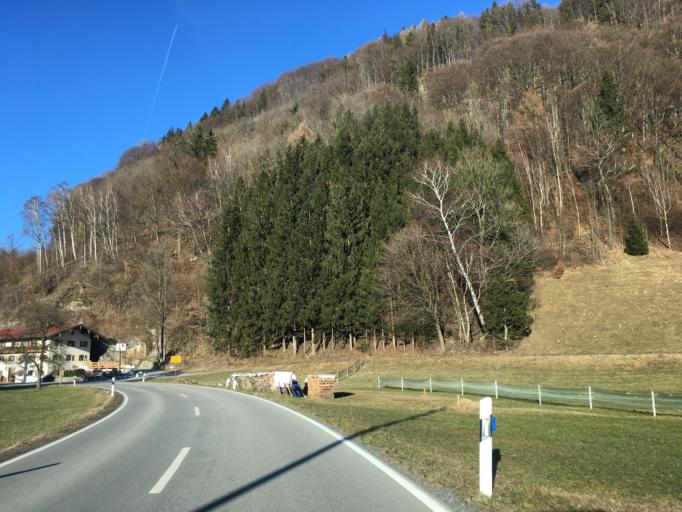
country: AT
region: Tyrol
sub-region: Politischer Bezirk Kufstein
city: Erl
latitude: 47.7092
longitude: 12.1652
